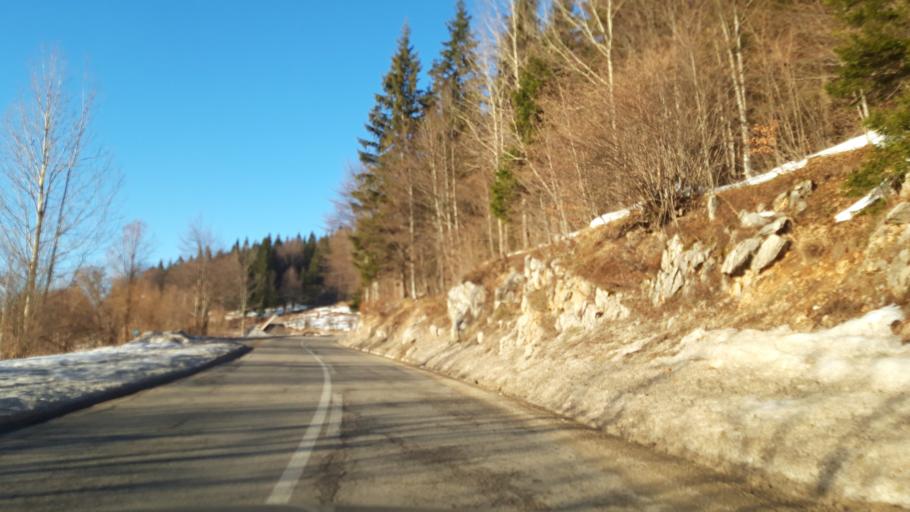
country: BA
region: Republika Srpska
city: Vlasenica
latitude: 44.1358
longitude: 18.9541
